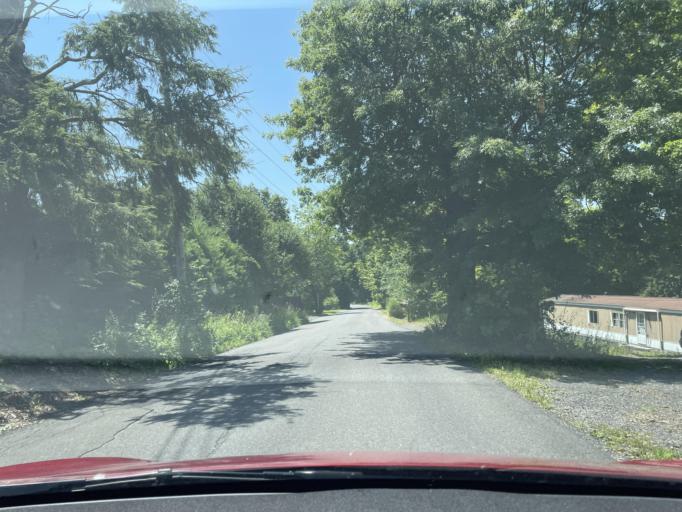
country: US
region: New York
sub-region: Ulster County
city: Lake Katrine
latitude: 42.0152
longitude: -73.9767
